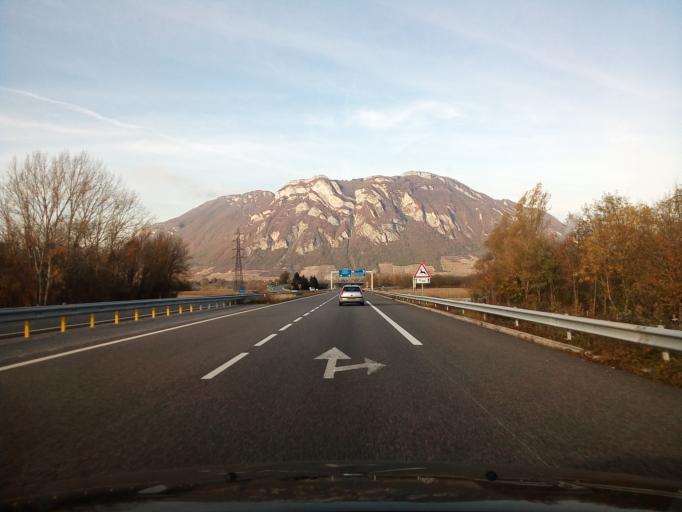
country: FR
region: Rhone-Alpes
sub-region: Departement de la Savoie
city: Les Marches
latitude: 45.4779
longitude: 6.0200
